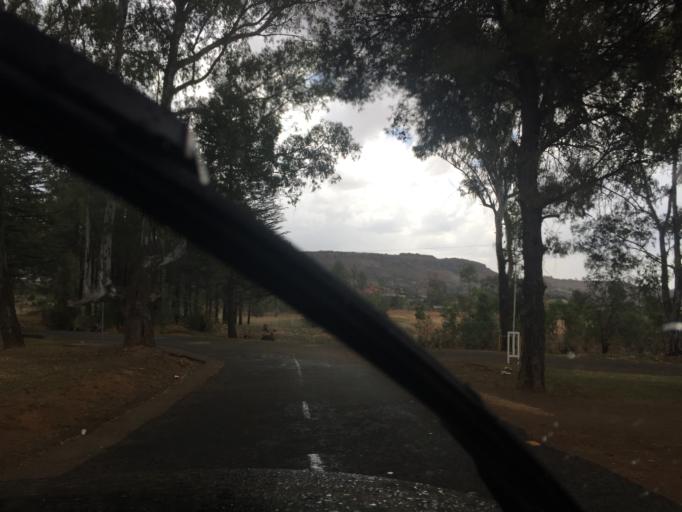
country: LS
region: Maseru
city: Nako
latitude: -29.4477
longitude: 27.7205
